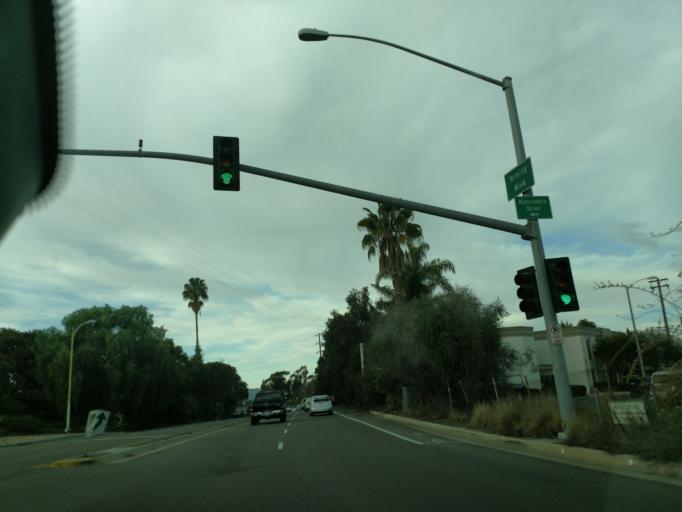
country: US
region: California
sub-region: San Diego County
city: Coronado
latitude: 32.7395
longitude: -117.2316
